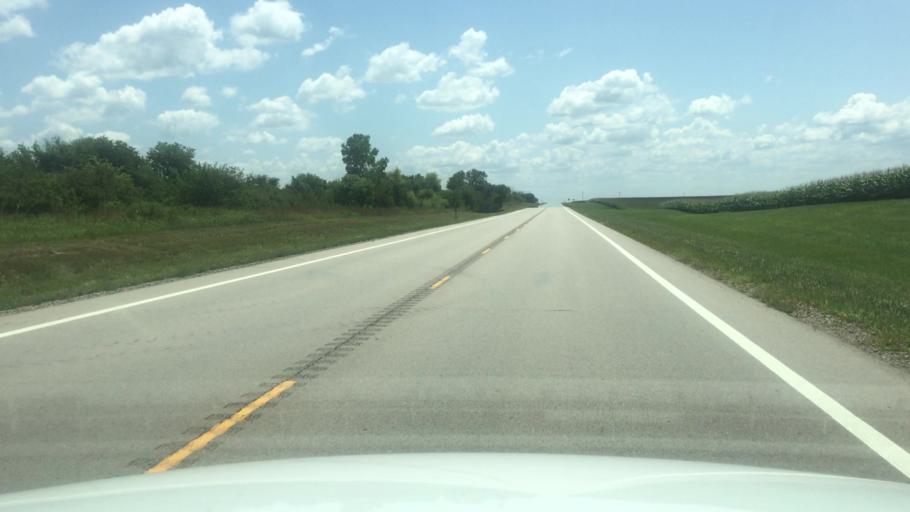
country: US
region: Kansas
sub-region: Brown County
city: Horton
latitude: 39.6455
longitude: -95.3551
